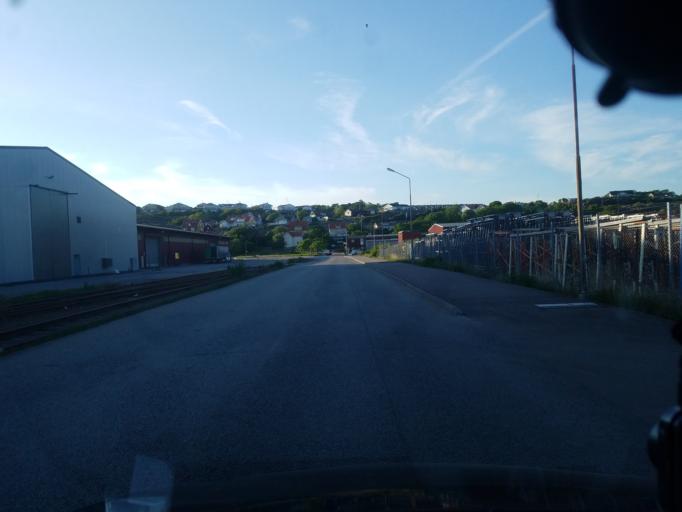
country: SE
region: Vaestra Goetaland
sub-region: Lysekils Kommun
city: Lysekil
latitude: 58.2750
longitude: 11.4535
